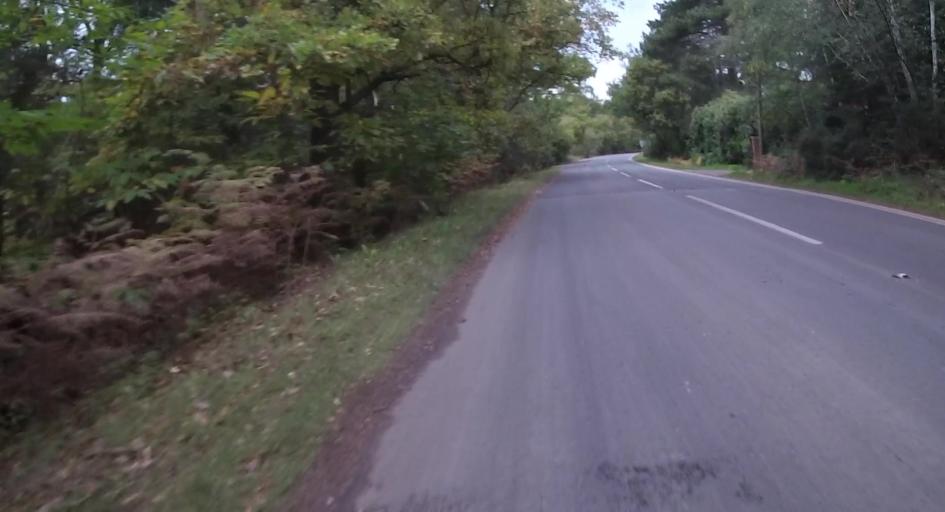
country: GB
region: England
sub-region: Wokingham
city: Finchampstead
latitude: 51.3642
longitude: -0.8376
